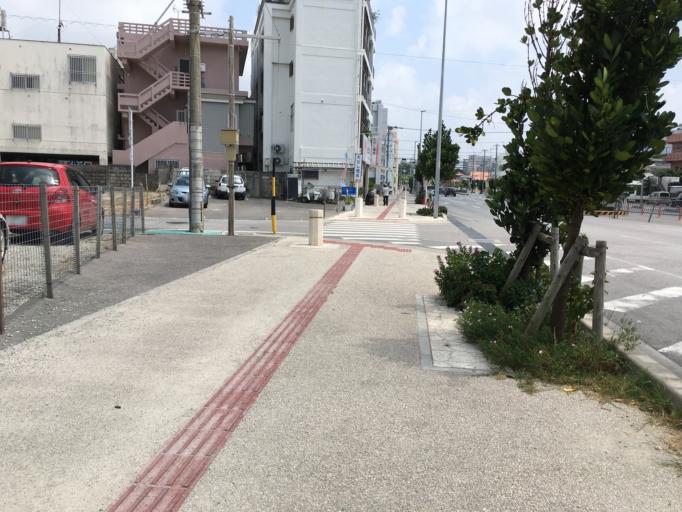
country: JP
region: Okinawa
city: Naha-shi
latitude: 26.2214
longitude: 127.6743
